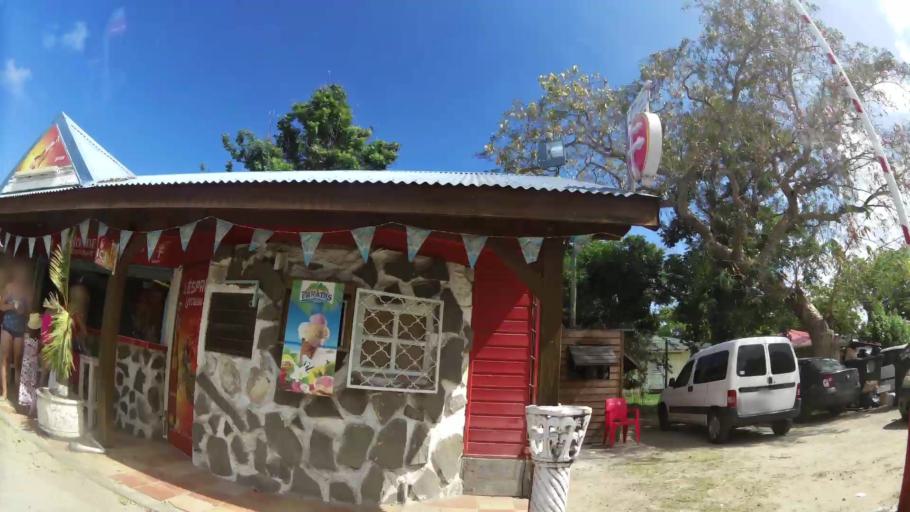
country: MQ
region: Martinique
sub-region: Martinique
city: Le Marin
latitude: 14.4412
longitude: -60.8802
